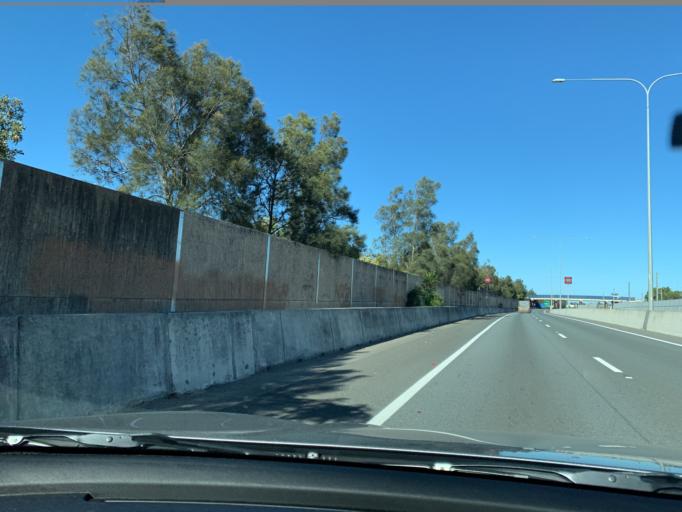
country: AU
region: Queensland
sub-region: Brisbane
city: Wynnum West
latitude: -27.4486
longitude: 153.1225
